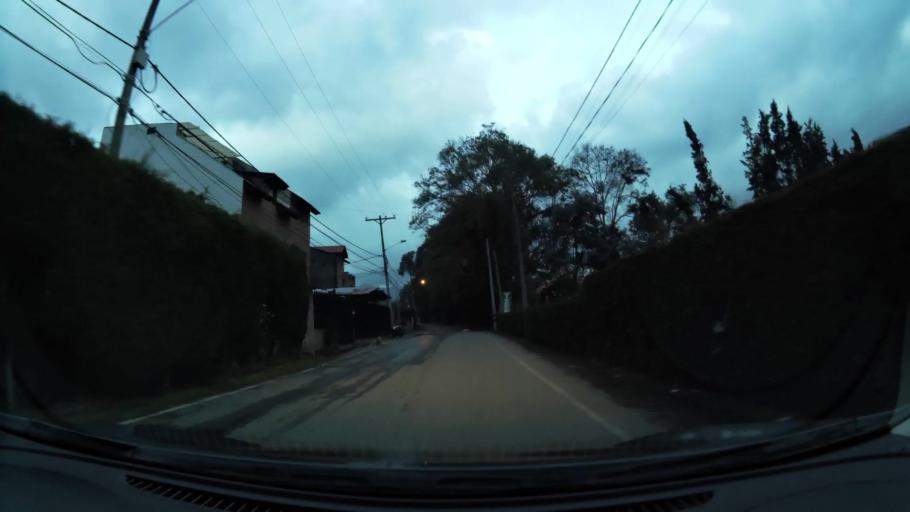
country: CO
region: Cundinamarca
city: Chia
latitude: 4.8380
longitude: -74.0725
